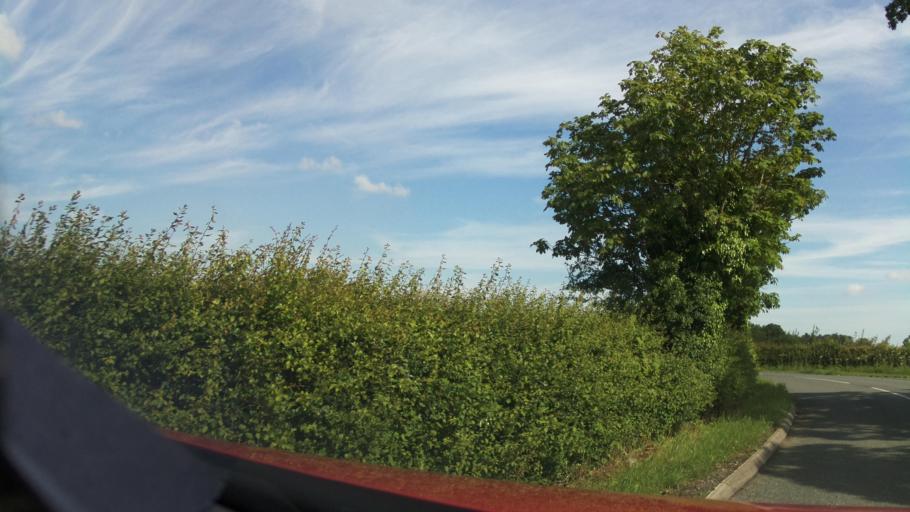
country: GB
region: England
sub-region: Lincolnshire
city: Skellingthorpe
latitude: 53.1462
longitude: -0.6313
